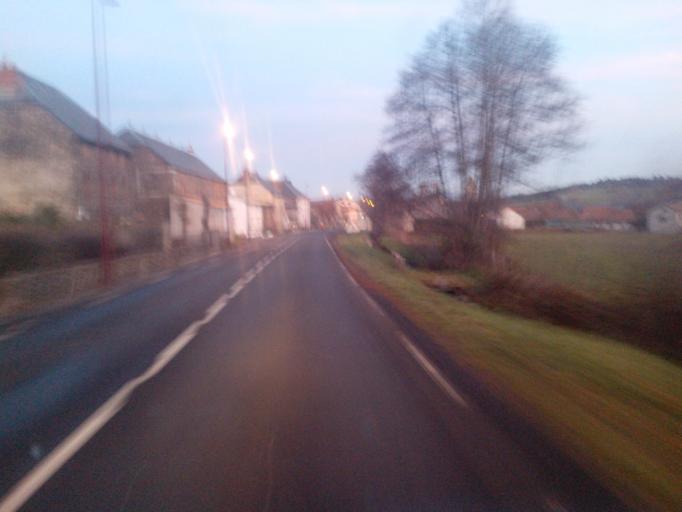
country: FR
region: Auvergne
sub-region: Departement du Cantal
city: Saint-Flour
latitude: 45.0523
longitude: 3.0357
